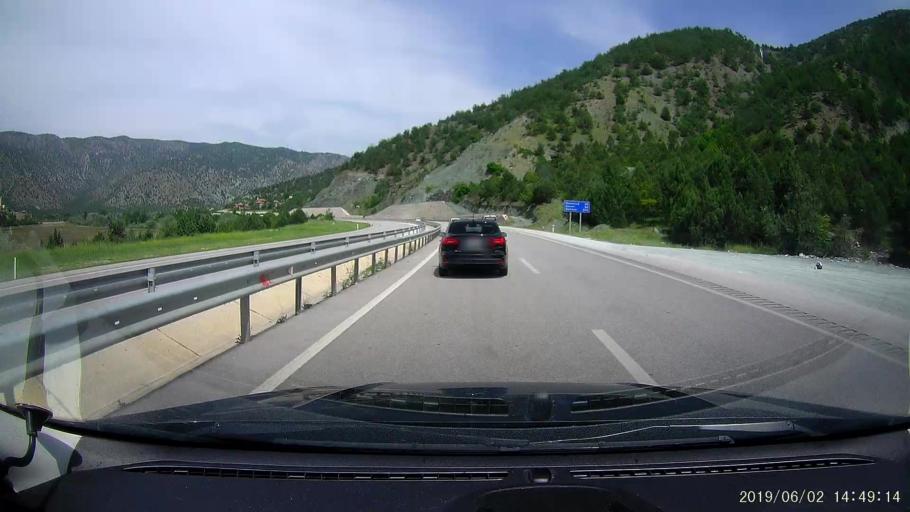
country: TR
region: Corum
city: Hacihamza
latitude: 41.0649
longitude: 34.4983
